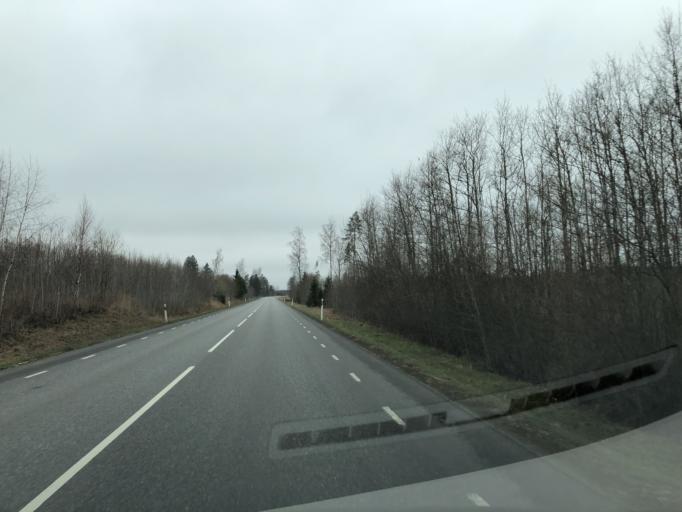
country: EE
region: Laeaene-Virumaa
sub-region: Rakke vald
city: Rakke
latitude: 59.0253
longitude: 26.2431
